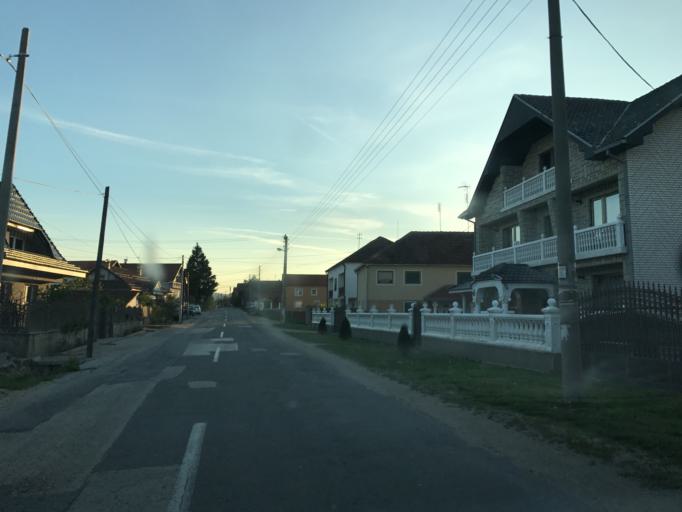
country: RO
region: Mehedinti
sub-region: Comuna Burila Mare
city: Burila Mare
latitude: 44.4931
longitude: 22.4871
